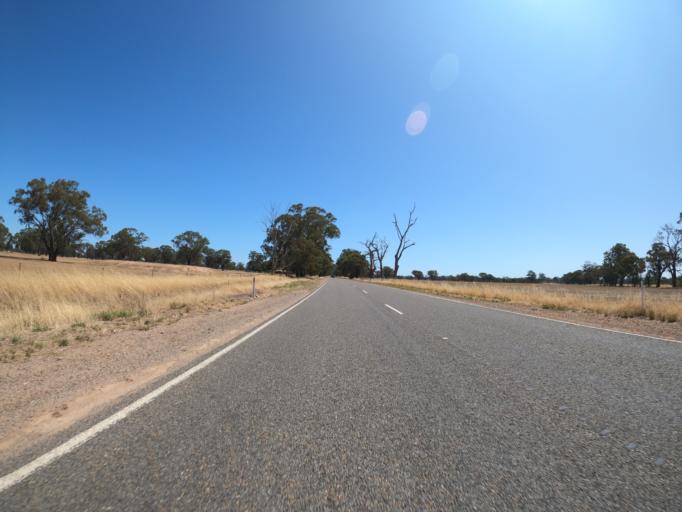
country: AU
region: New South Wales
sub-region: Corowa Shire
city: Corowa
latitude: -36.0673
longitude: 146.3613
